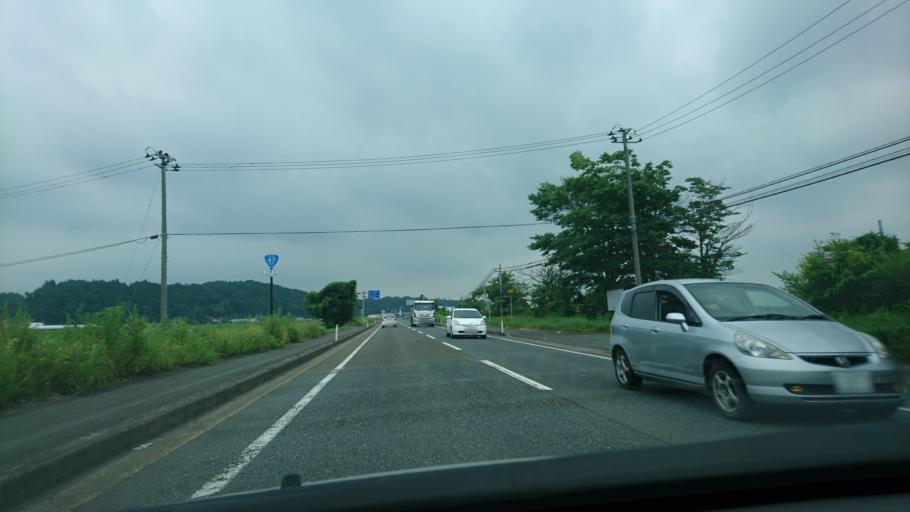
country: JP
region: Miyagi
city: Furukawa
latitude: 38.6607
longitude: 140.8755
